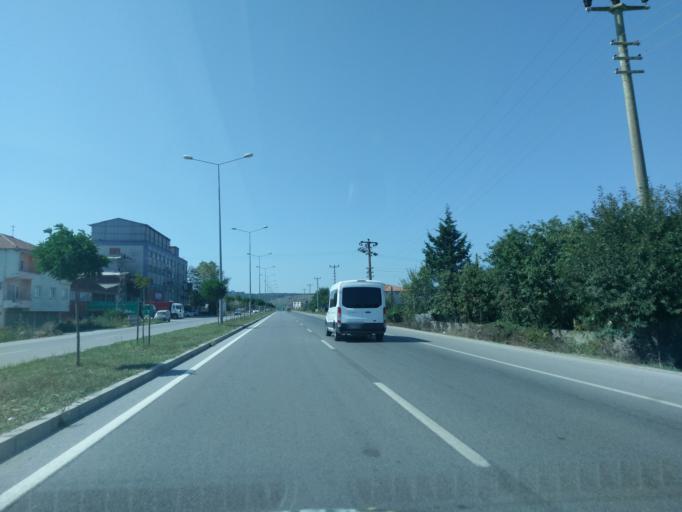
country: TR
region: Samsun
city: Bafra
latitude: 41.5731
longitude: 35.8677
